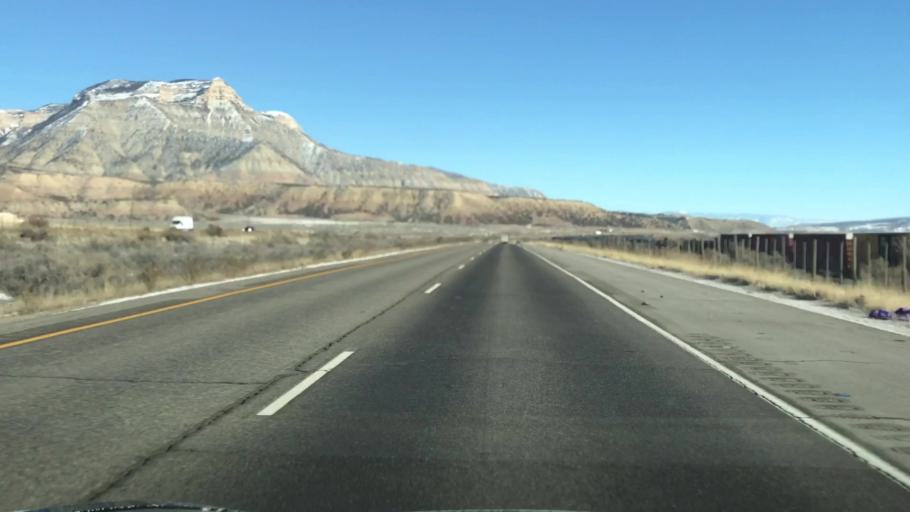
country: US
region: Colorado
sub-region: Garfield County
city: Battlement Mesa
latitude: 39.4700
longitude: -108.0272
